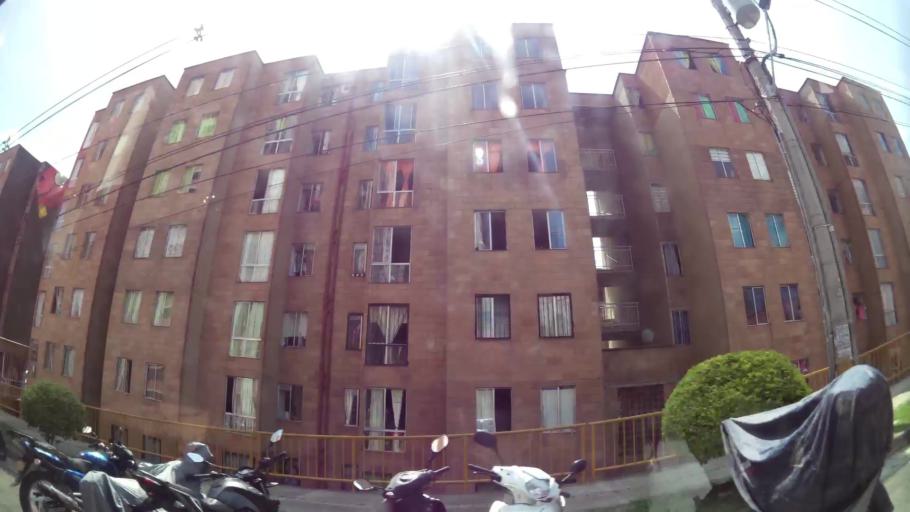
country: CO
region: Antioquia
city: La Estrella
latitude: 6.1752
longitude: -75.6475
